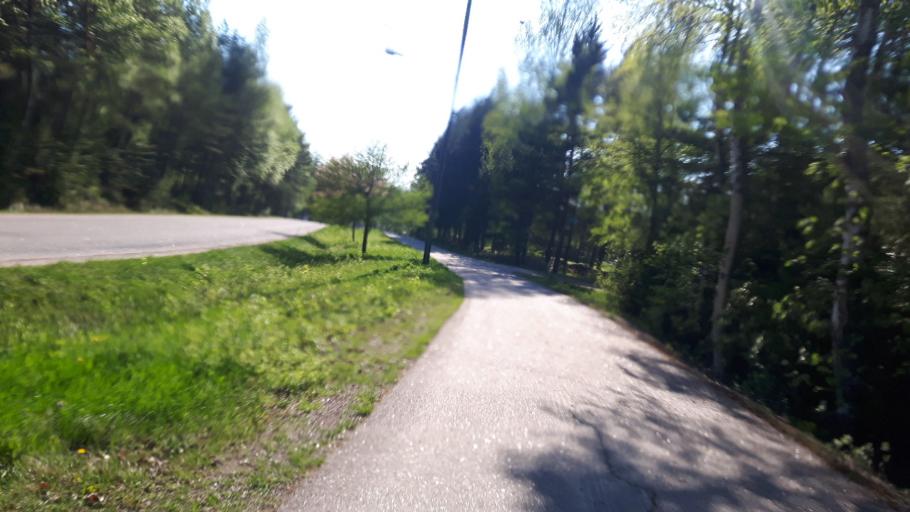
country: FI
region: Kymenlaakso
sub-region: Kotka-Hamina
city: Kotka
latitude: 60.4386
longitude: 26.8680
